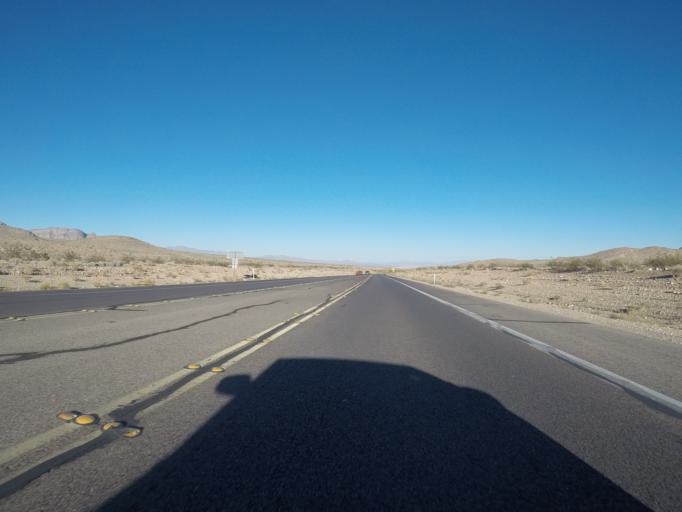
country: US
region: Nevada
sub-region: Clark County
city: Summerlin South
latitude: 36.1420
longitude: -115.3985
